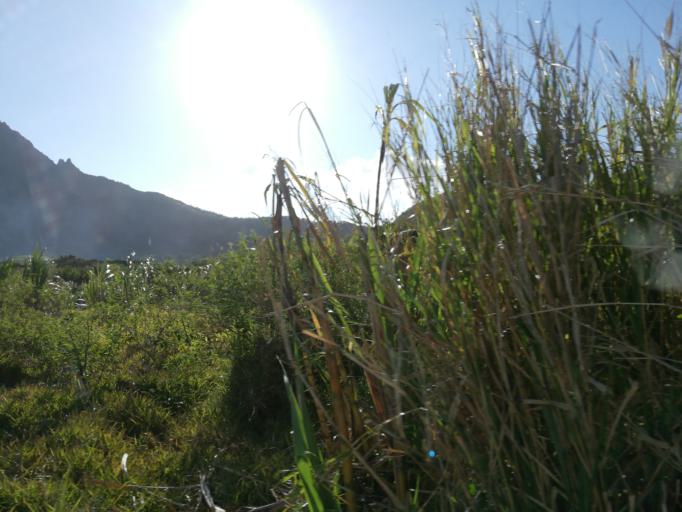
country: MU
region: Moka
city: Saint Pierre
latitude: -20.2088
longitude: 57.5262
